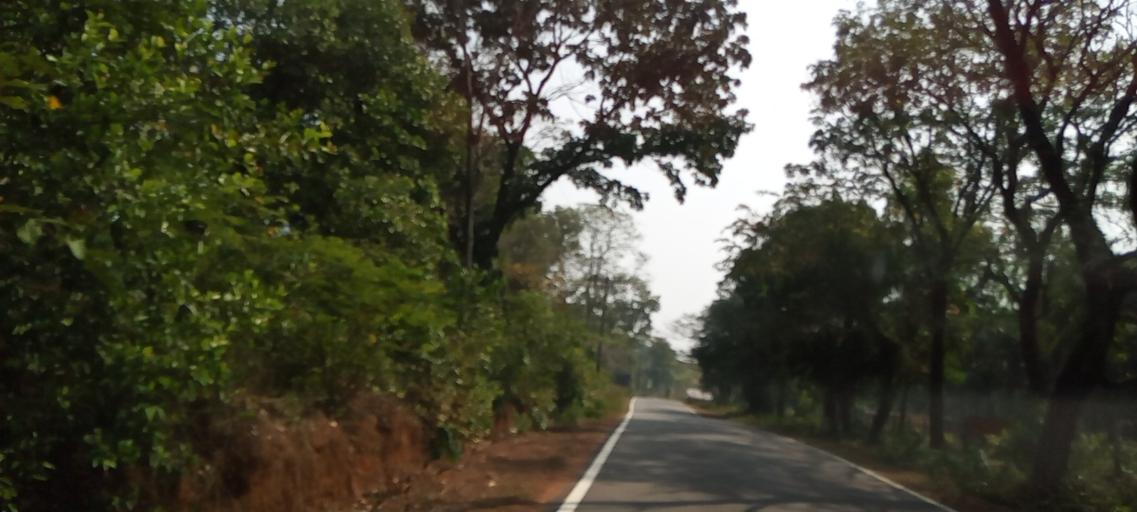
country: IN
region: Karnataka
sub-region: Udupi
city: Hosangadi
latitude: 13.5417
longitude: 74.9101
